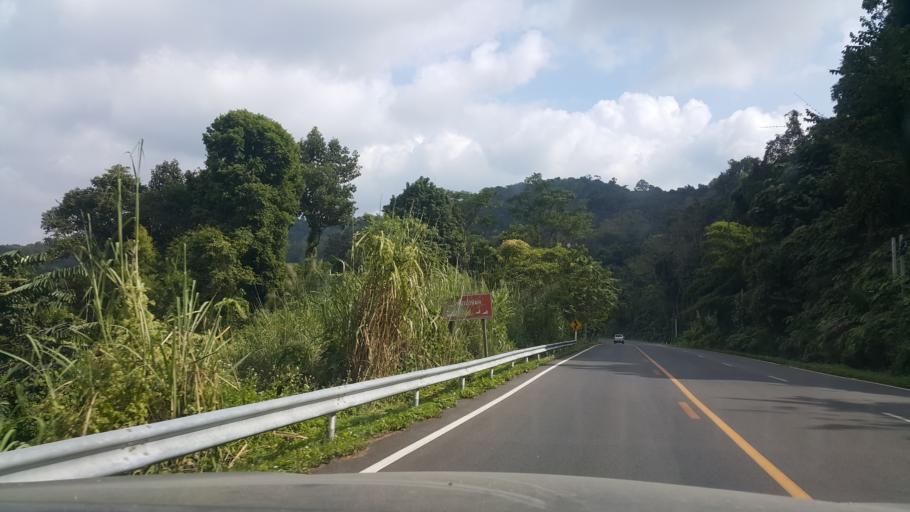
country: TH
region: Phayao
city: Phayao
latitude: 19.0589
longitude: 99.7850
